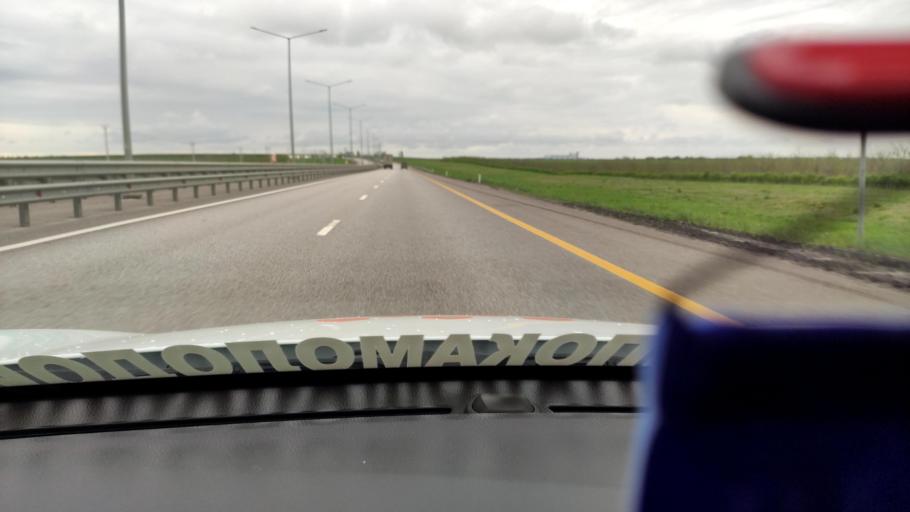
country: RU
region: Voronezj
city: Novaya Usman'
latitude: 51.5954
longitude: 39.3594
